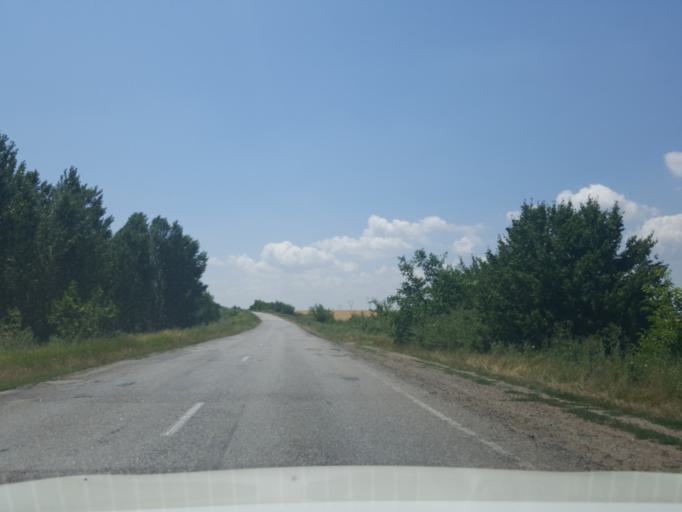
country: UA
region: Odessa
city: Starokozache
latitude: 46.3965
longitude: 30.0951
